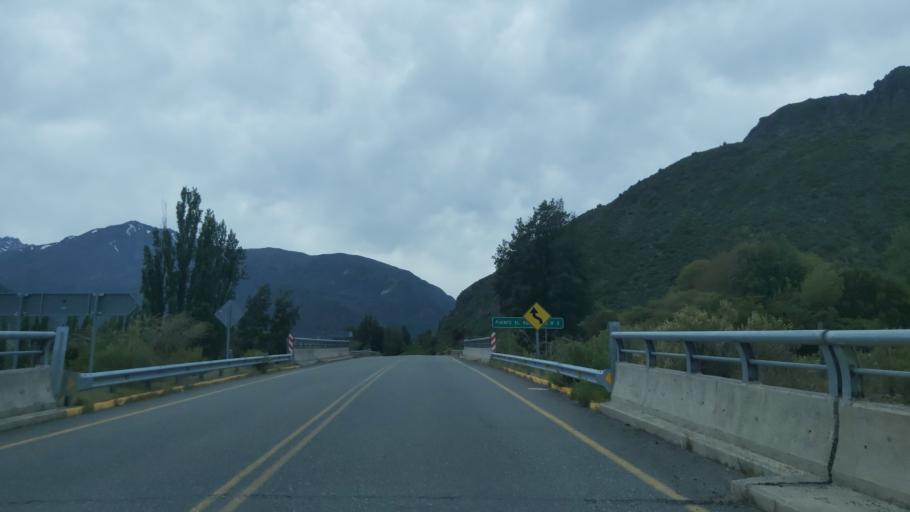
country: CL
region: Maule
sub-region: Provincia de Linares
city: Colbun
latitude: -35.8123
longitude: -70.8721
